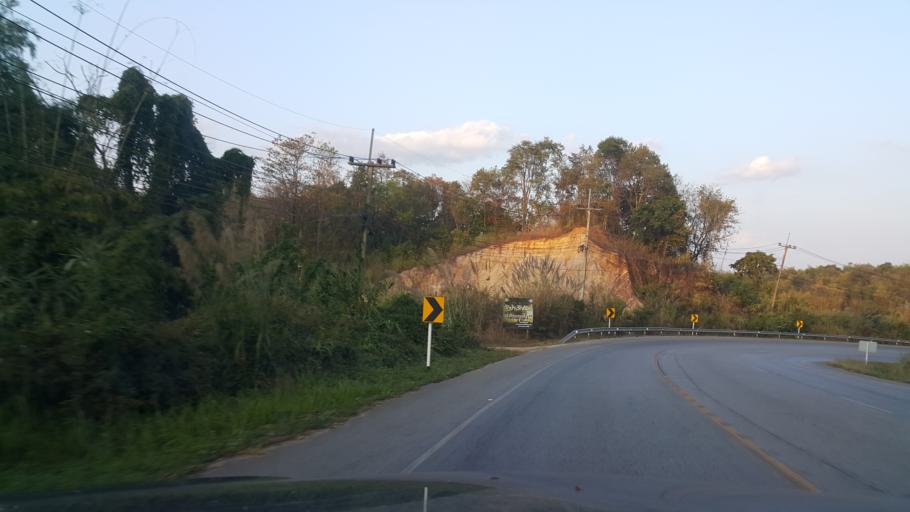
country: TH
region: Loei
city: Phu Ruea
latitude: 17.4735
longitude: 101.5386
